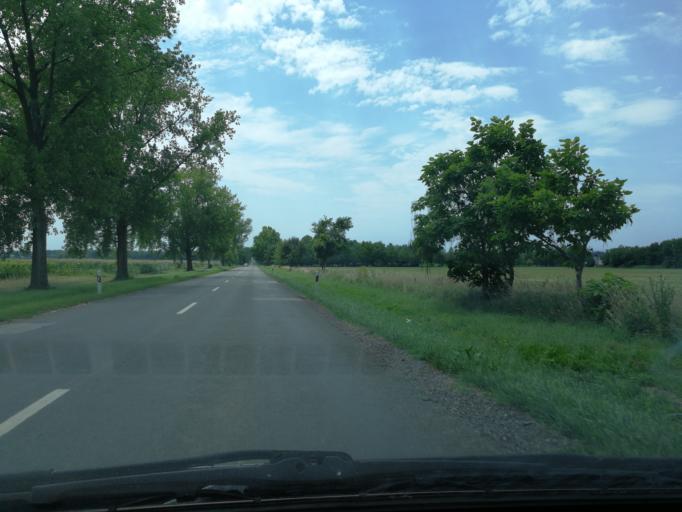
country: HU
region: Baranya
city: Harkany
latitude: 45.8738
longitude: 18.2328
